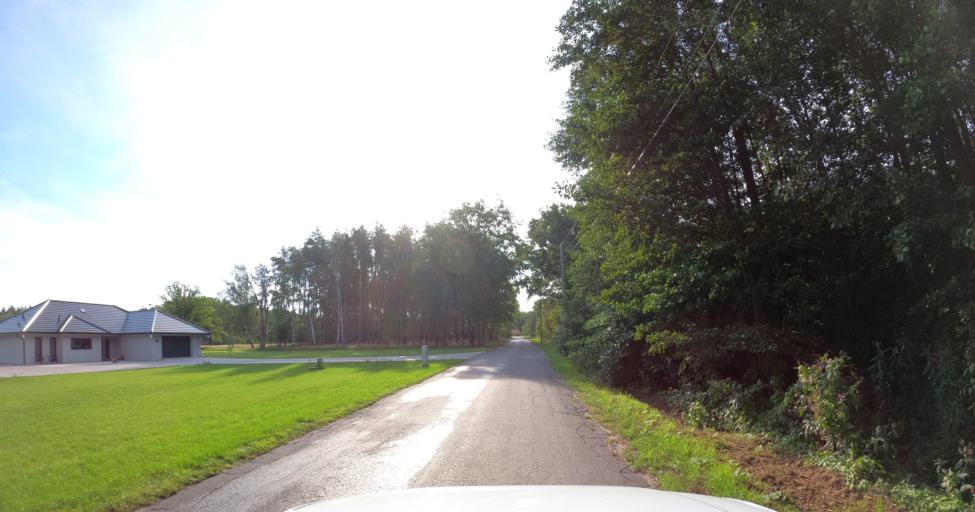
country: PL
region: West Pomeranian Voivodeship
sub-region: Powiat goleniowski
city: Goleniow
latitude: 53.5117
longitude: 14.7357
